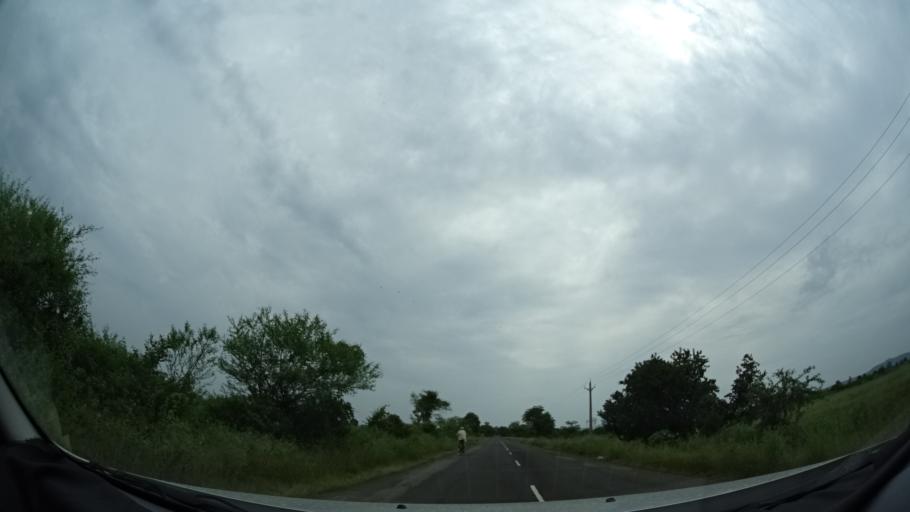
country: IN
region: Madhya Pradesh
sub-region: Raisen
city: Sultanpur
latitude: 23.3107
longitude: 78.0465
